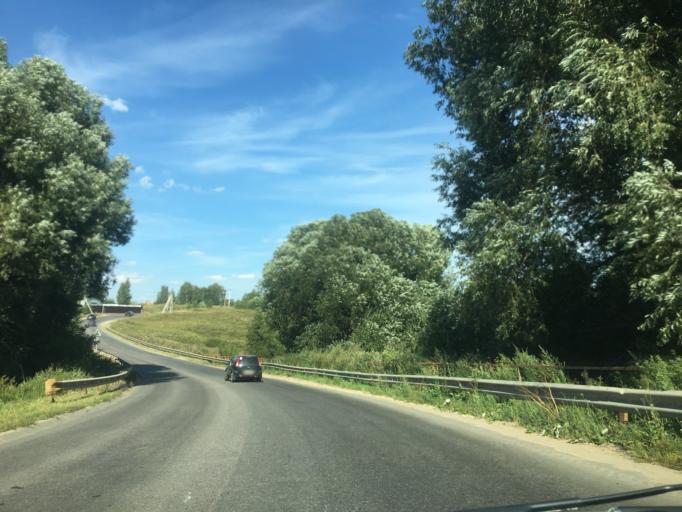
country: RU
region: Moskovskaya
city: Vidnoye
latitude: 55.5027
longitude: 37.6758
